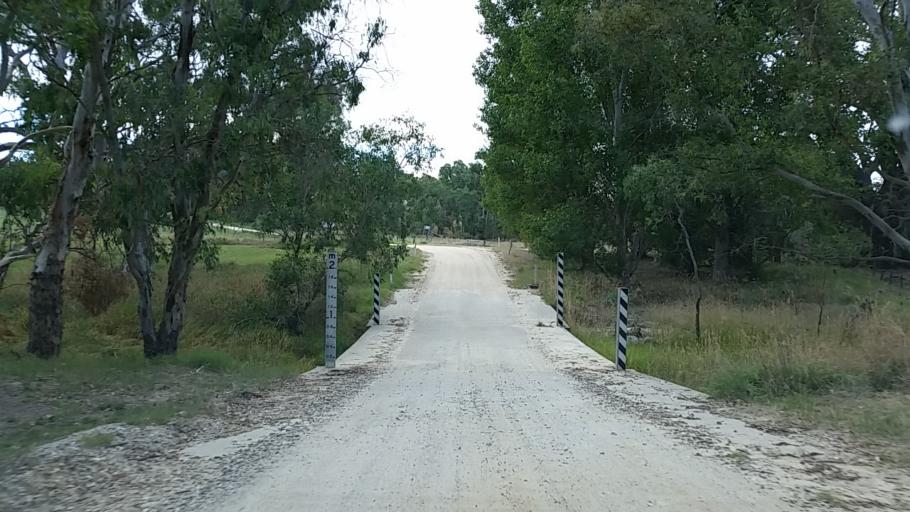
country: AU
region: South Australia
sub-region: Barossa
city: Angaston
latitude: -34.5652
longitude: 139.0815
